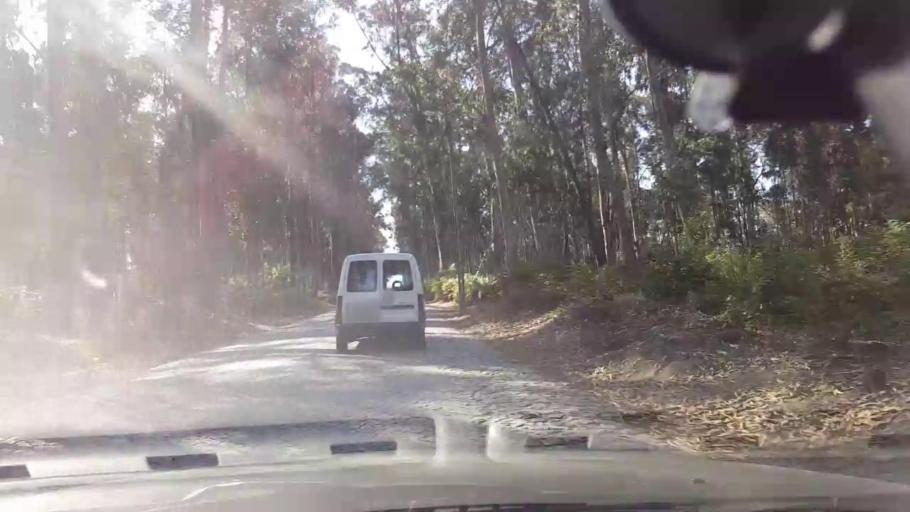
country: PT
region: Porto
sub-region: Vila do Conde
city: Arvore
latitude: 41.3565
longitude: -8.6894
